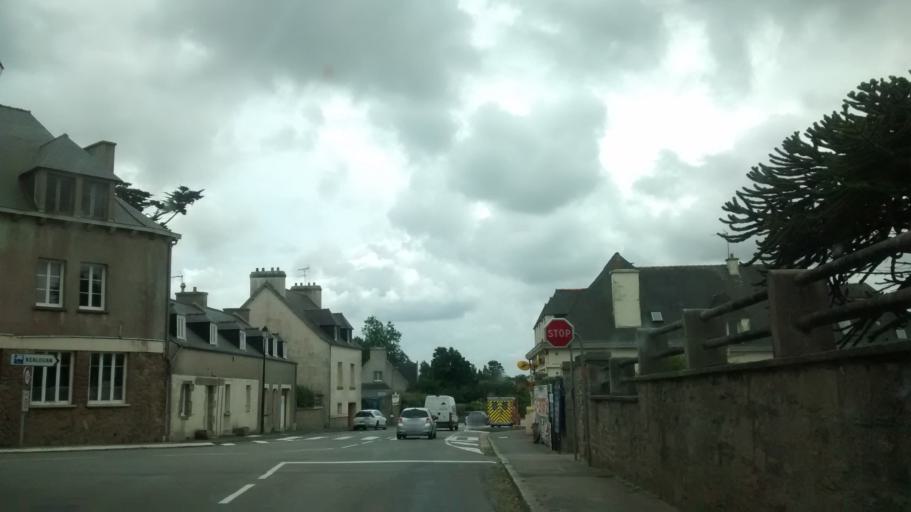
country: FR
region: Brittany
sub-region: Departement du Finistere
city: Guisseny
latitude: 48.6343
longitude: -4.4109
